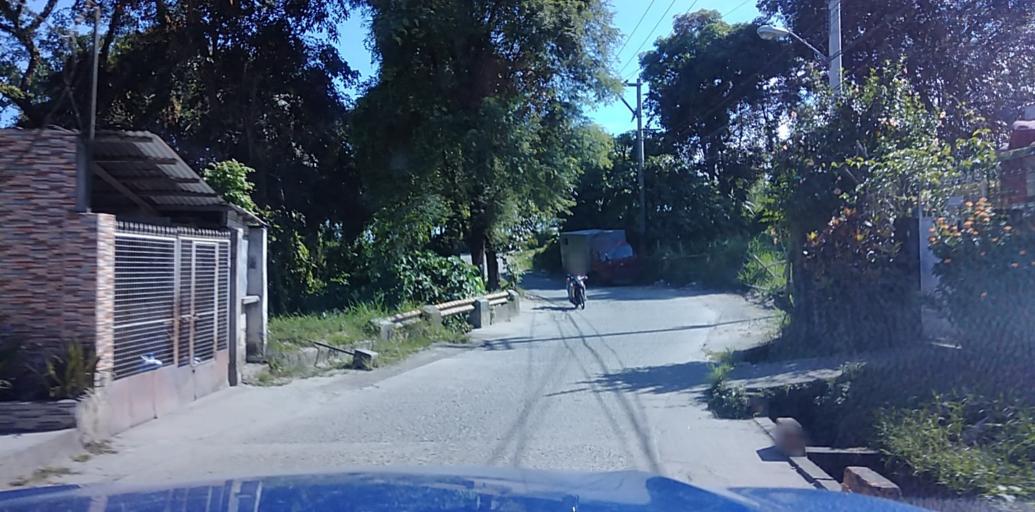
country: PH
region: Central Luzon
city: Santol
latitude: 15.1710
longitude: 120.5155
